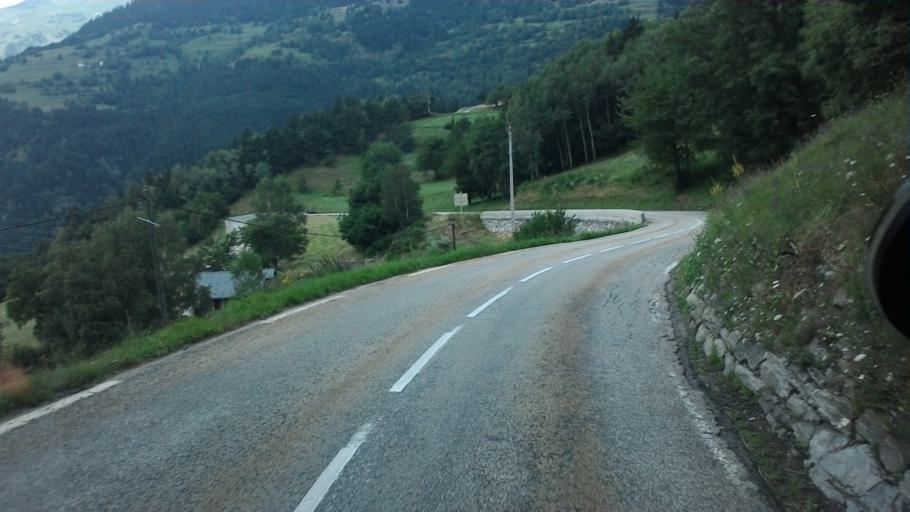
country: FR
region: Rhone-Alpes
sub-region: Departement de la Savoie
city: Seez
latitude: 45.6252
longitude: 6.8183
